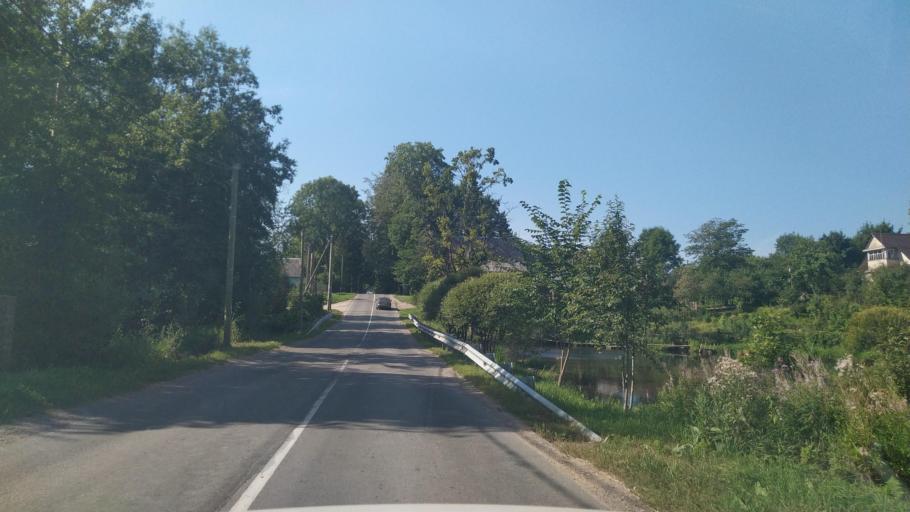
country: RU
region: Leningrad
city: Siverskiy
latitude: 59.2923
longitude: 30.0669
